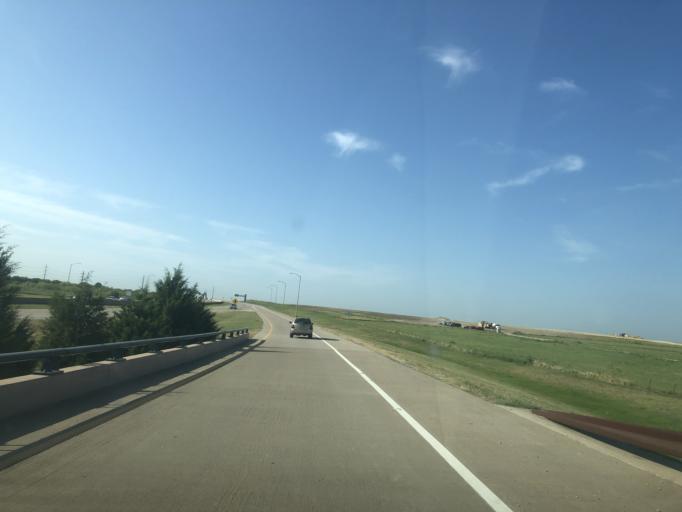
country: US
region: Texas
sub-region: Tarrant County
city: Benbrook
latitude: 32.6442
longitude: -97.4169
